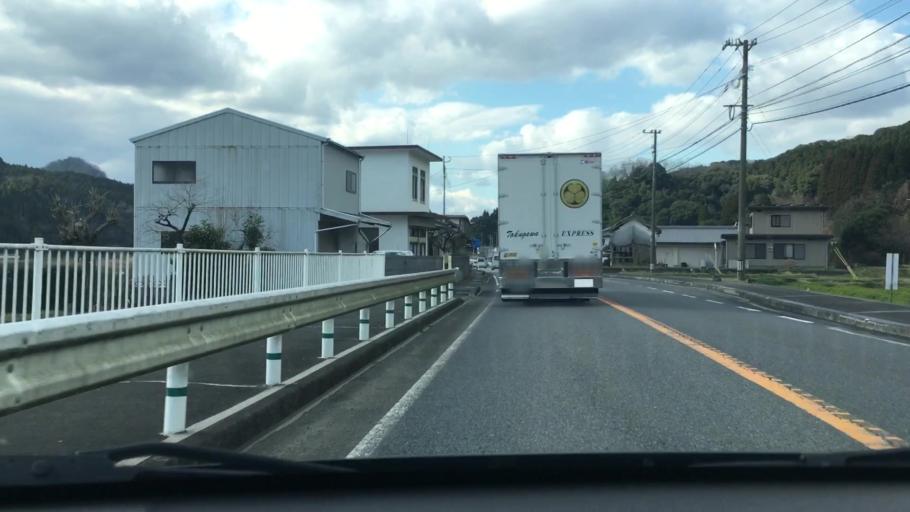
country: JP
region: Oita
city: Usuki
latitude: 33.0057
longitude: 131.7240
